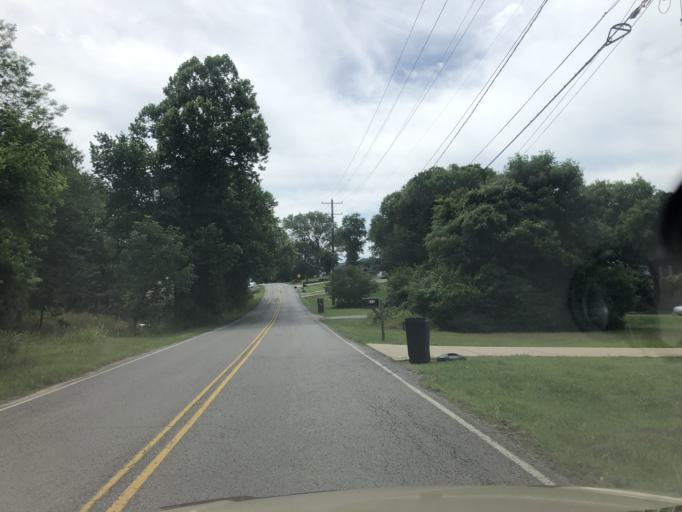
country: US
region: Tennessee
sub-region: Davidson County
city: Lakewood
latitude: 36.2598
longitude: -86.6187
